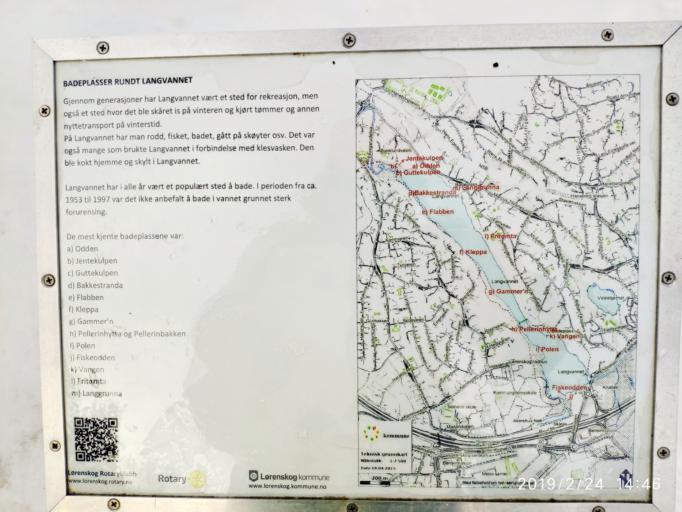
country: NO
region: Akershus
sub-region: Lorenskog
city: Kjenn
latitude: 59.9326
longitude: 10.9621
